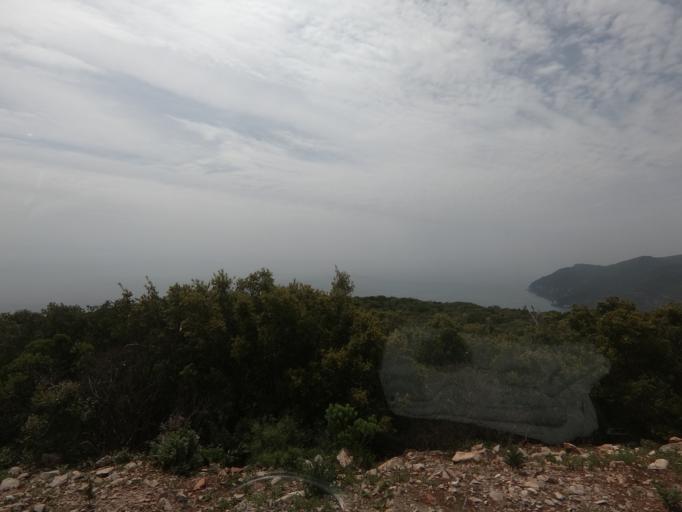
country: PT
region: Setubal
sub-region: Palmela
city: Quinta do Anjo
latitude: 38.4912
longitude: -8.9594
